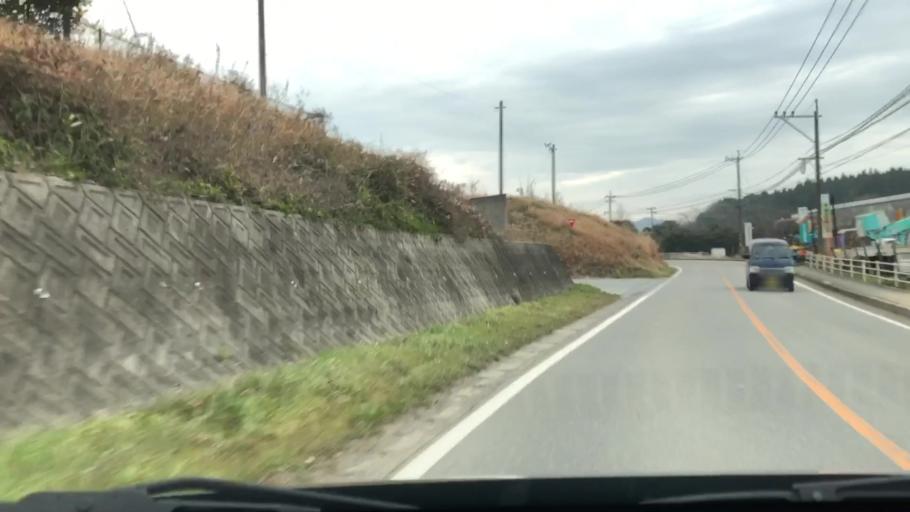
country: JP
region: Oita
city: Usuki
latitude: 33.0190
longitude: 131.6757
